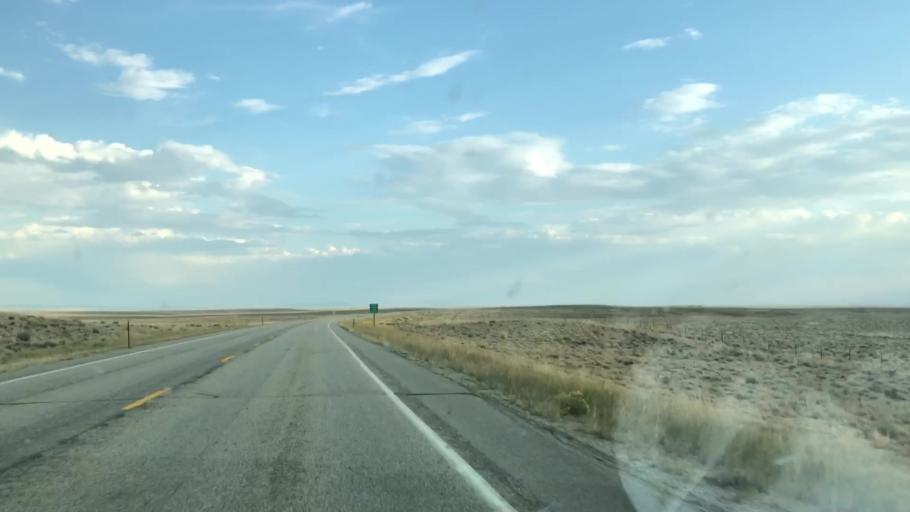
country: US
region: Wyoming
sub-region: Sweetwater County
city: North Rock Springs
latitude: 42.2586
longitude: -109.4706
